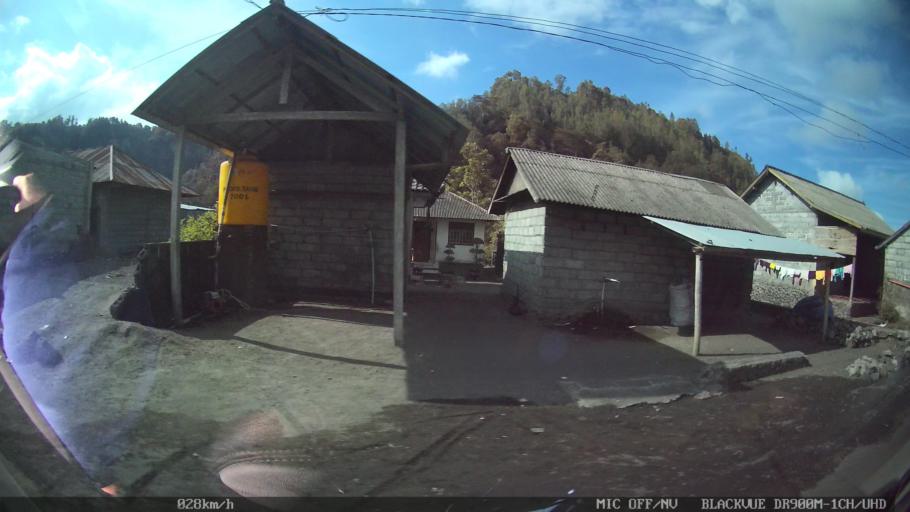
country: ID
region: Bali
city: Banjar Trunyan
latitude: -8.2156
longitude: 115.3734
